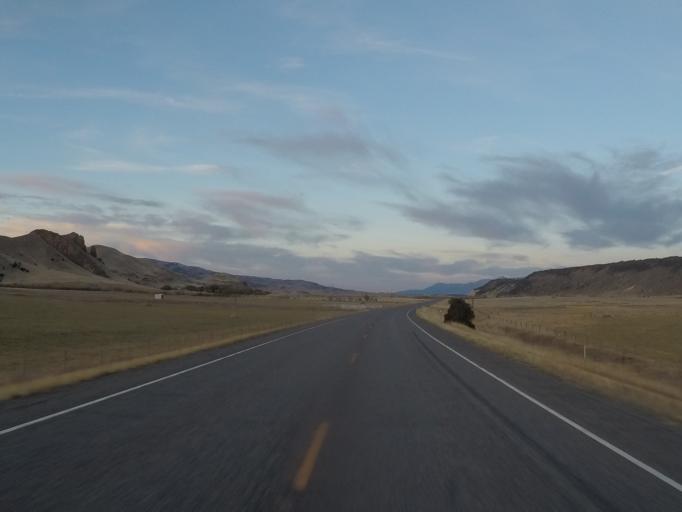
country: US
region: Montana
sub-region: Gallatin County
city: Bozeman
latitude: 45.2759
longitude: -110.8568
